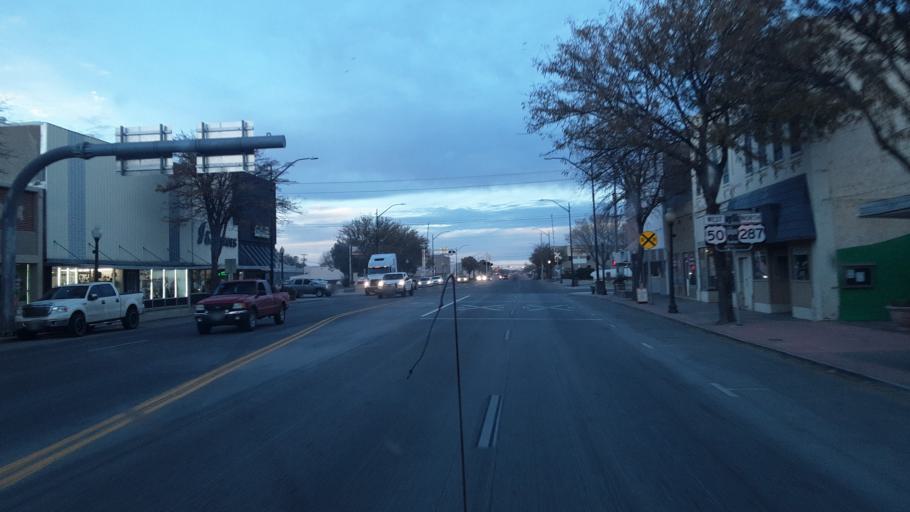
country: US
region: Colorado
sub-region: Prowers County
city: Lamar
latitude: 38.0885
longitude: -102.6192
